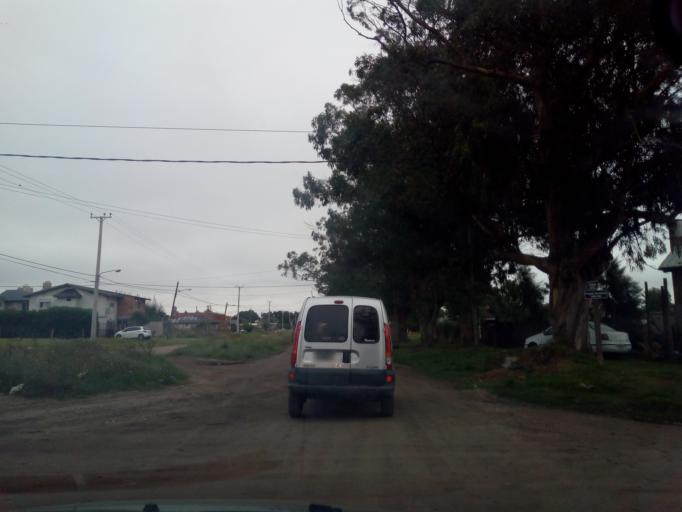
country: AR
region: Buenos Aires
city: Mar del Plata
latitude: -38.0690
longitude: -57.5714
